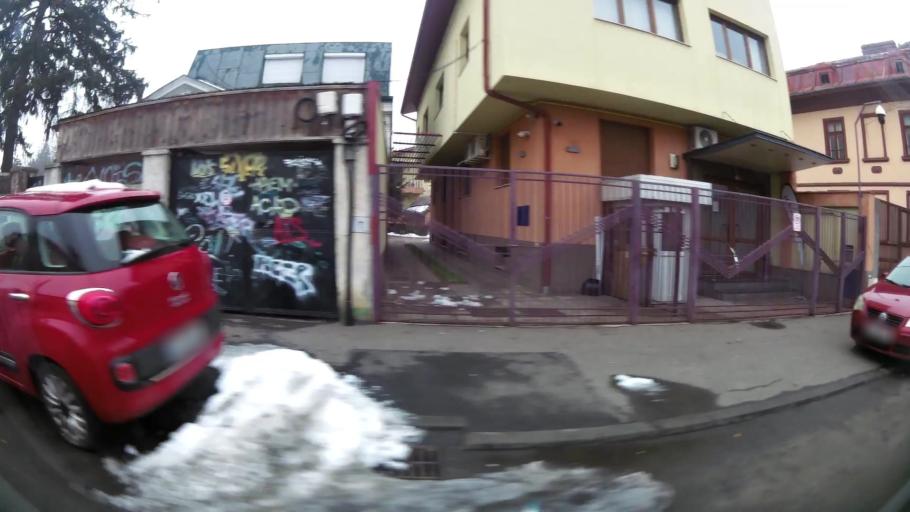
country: RO
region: Bucuresti
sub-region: Municipiul Bucuresti
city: Bucharest
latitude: 44.4401
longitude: 26.1194
